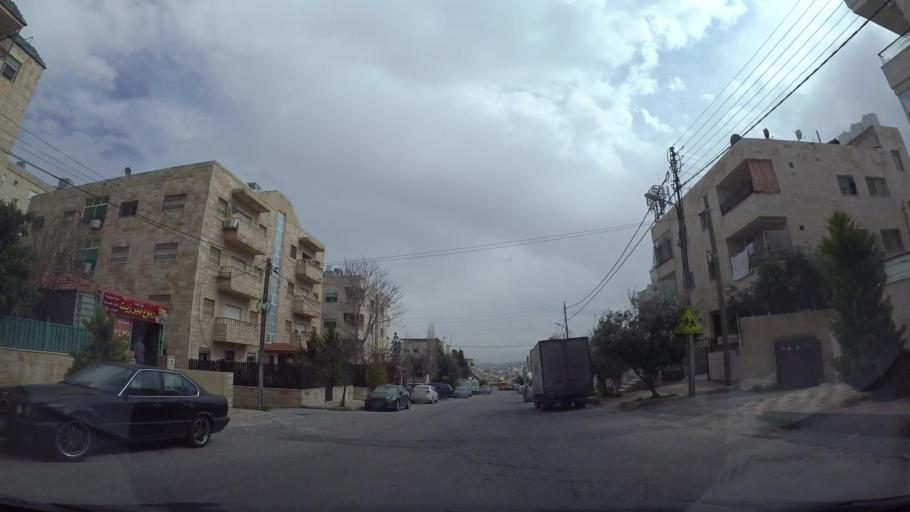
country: JO
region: Amman
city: Amman
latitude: 31.9996
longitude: 35.9375
